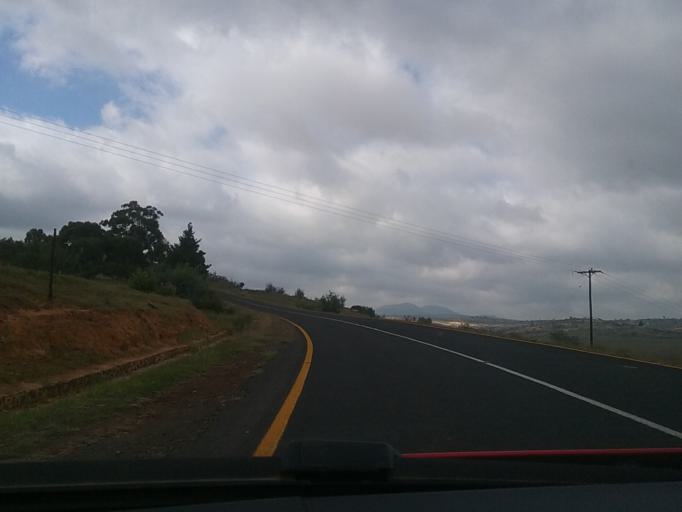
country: LS
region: Berea
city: Teyateyaneng
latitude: -29.1826
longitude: 27.7876
